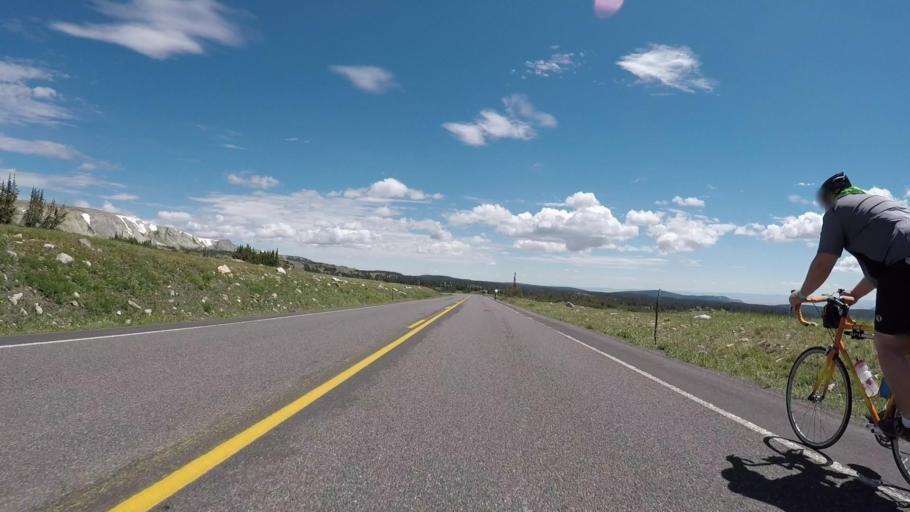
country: US
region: Wyoming
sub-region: Carbon County
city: Saratoga
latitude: 41.3445
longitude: -106.2918
